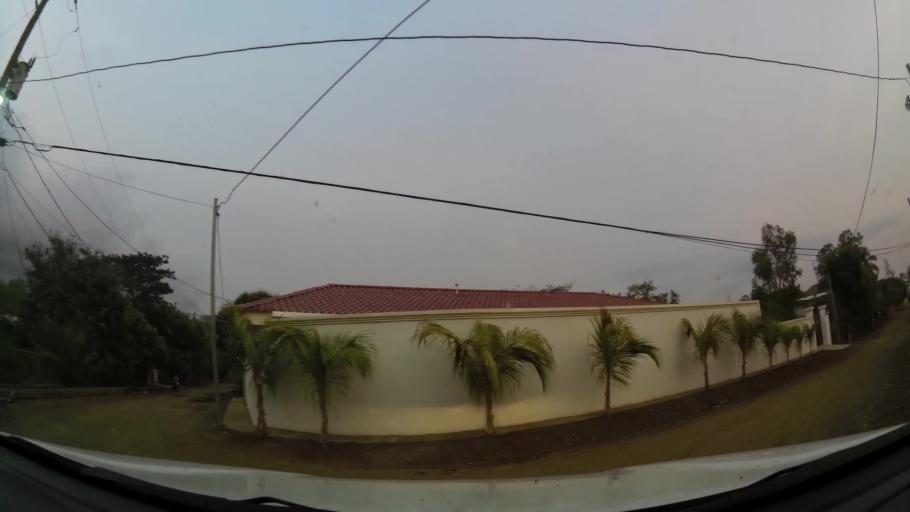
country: NI
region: Rivas
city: San Juan del Sur
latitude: 11.2633
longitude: -85.8766
